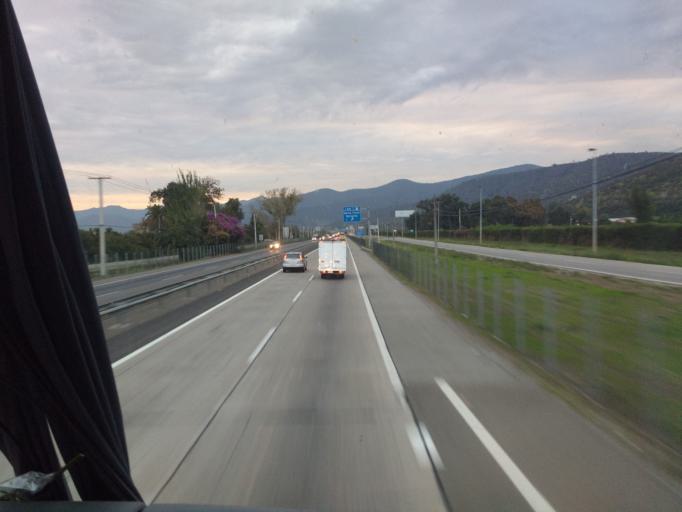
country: CL
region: Santiago Metropolitan
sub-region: Provincia de Chacabuco
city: Lampa
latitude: -33.4298
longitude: -71.0348
